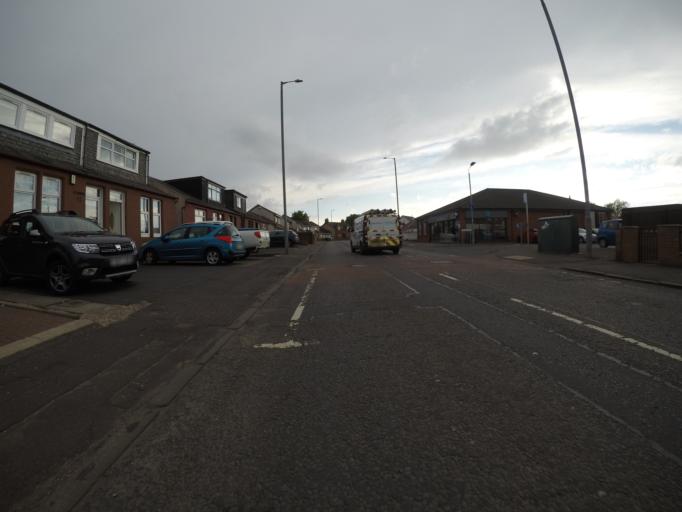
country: GB
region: Scotland
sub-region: North Ayrshire
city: Dreghorn
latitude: 55.6075
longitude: -4.6219
